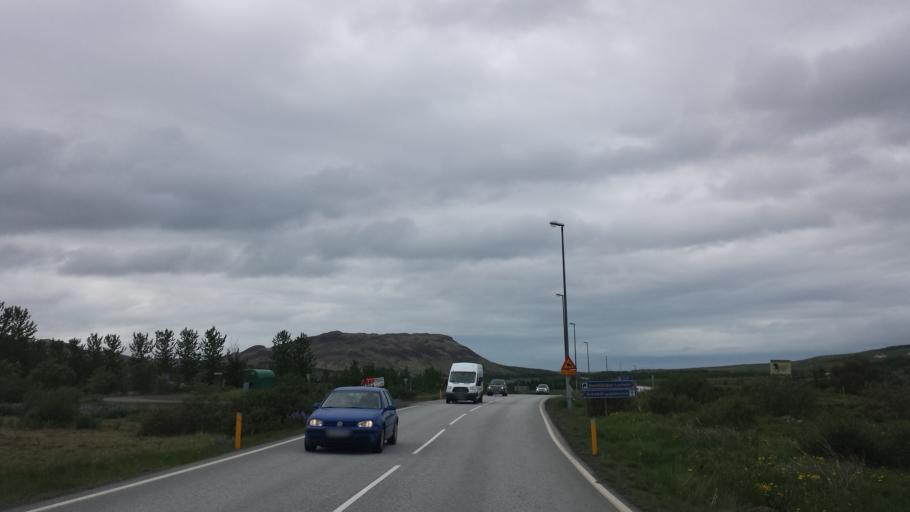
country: IS
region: Capital Region
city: Mosfellsbaer
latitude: 64.1805
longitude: -21.5887
